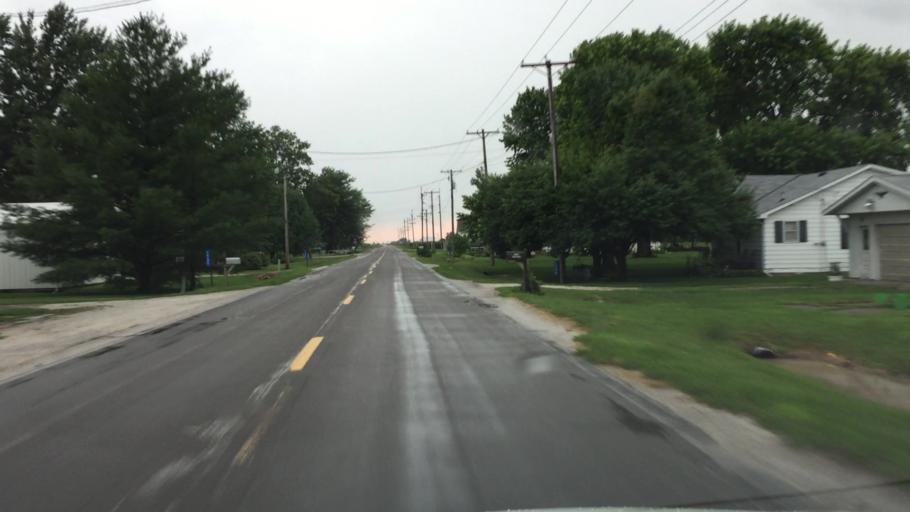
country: US
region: Illinois
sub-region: Hancock County
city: Carthage
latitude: 40.5207
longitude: -91.1684
